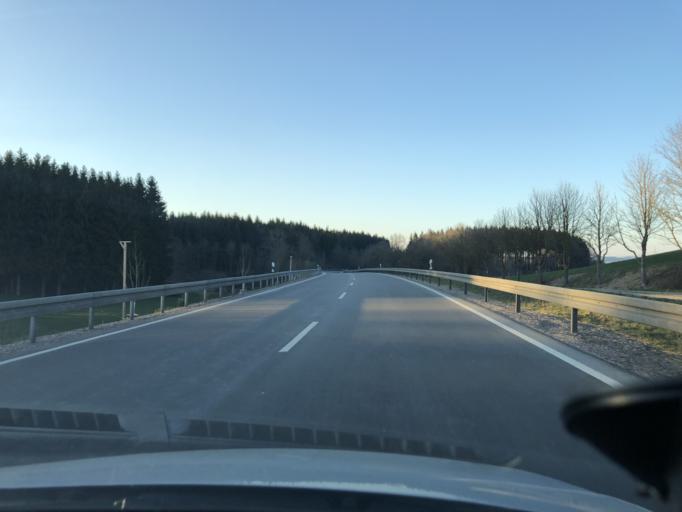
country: DE
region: Baden-Wuerttemberg
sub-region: Freiburg Region
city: Hufingen
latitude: 47.9000
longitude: 8.5087
